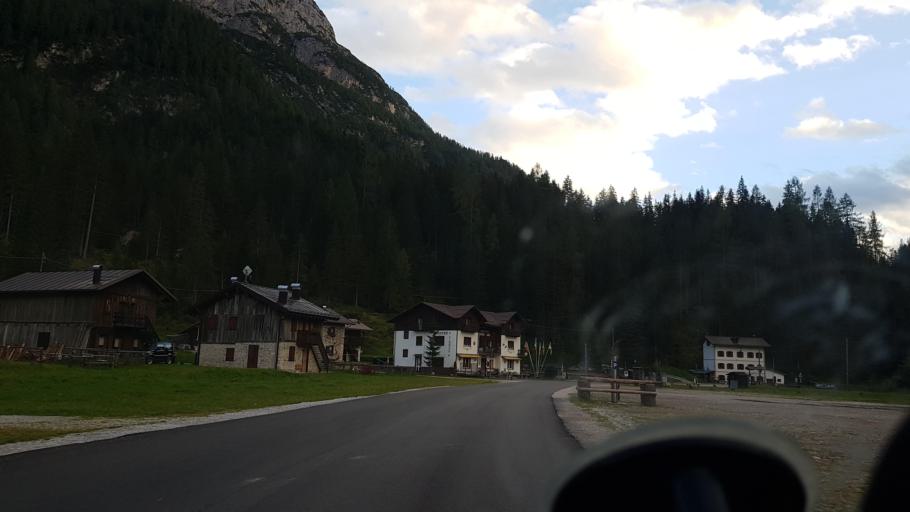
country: IT
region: Veneto
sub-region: Provincia di Belluno
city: San Pietro di Cadore
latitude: 46.6025
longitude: 12.6312
